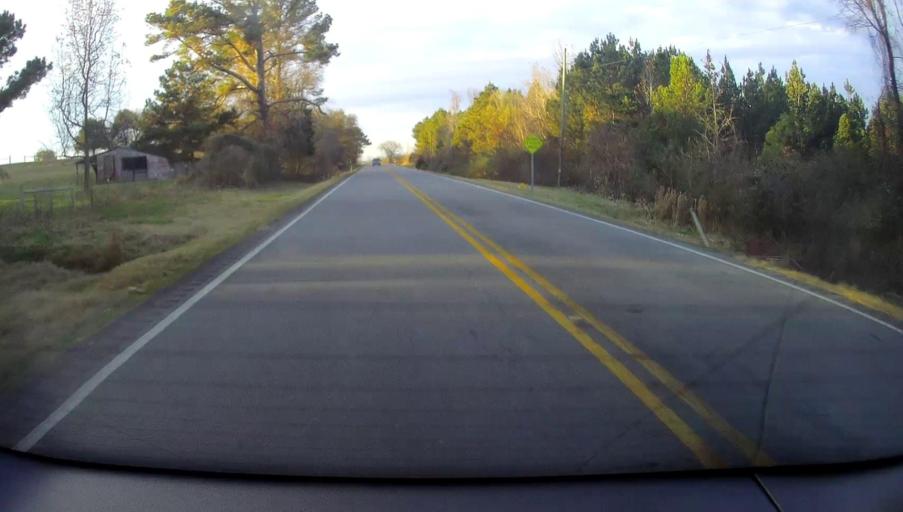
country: US
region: Alabama
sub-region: Blount County
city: Oneonta
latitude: 34.0897
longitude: -86.3508
